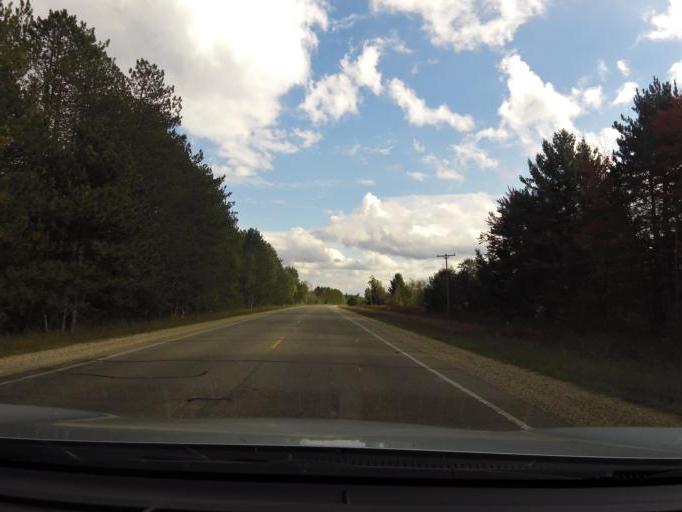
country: US
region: Michigan
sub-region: Roscommon County
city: Saint Helen
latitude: 44.3976
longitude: -84.4394
